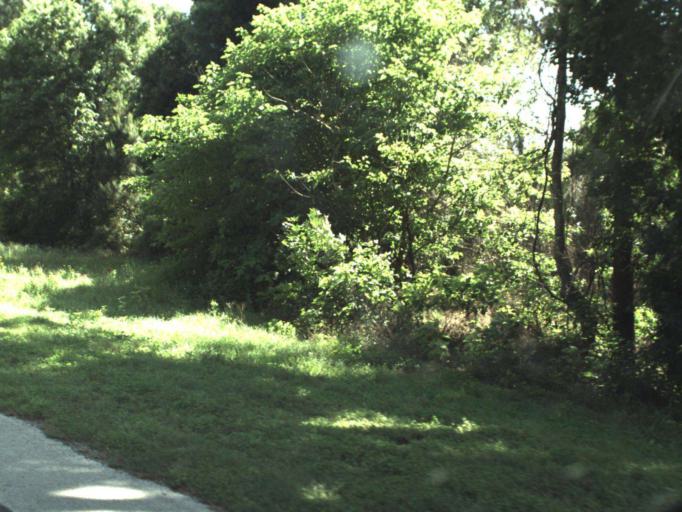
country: US
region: Florida
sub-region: Marion County
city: Belleview
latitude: 29.1040
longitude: -82.0915
